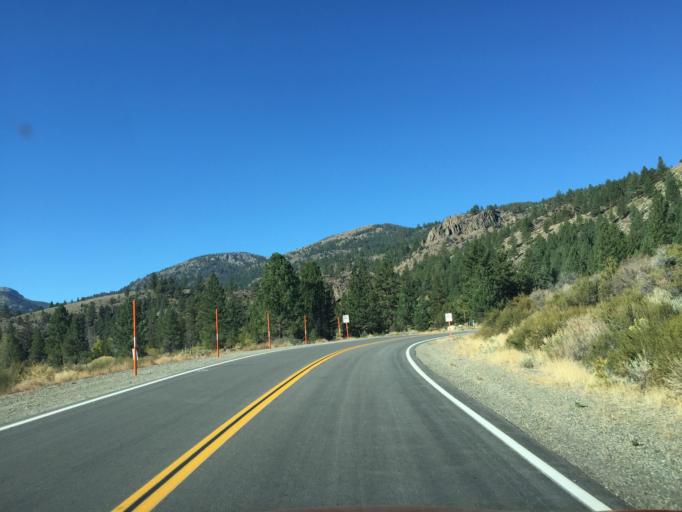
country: US
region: California
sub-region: Mono County
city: Bridgeport
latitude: 38.3507
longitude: -119.5312
